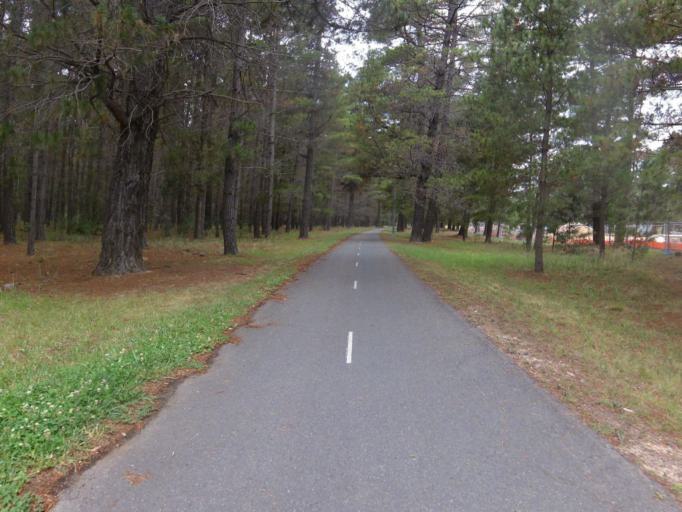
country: AU
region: Australian Capital Territory
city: Macarthur
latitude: -35.4117
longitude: 149.1228
